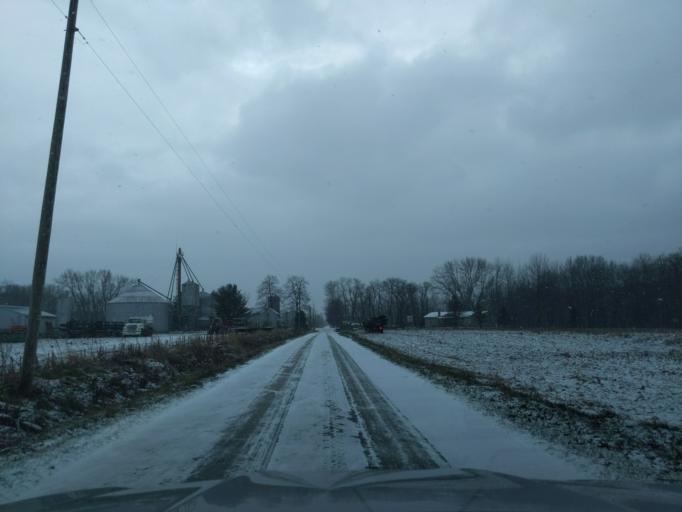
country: US
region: Indiana
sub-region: Decatur County
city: Westport
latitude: 39.2301
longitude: -85.4937
